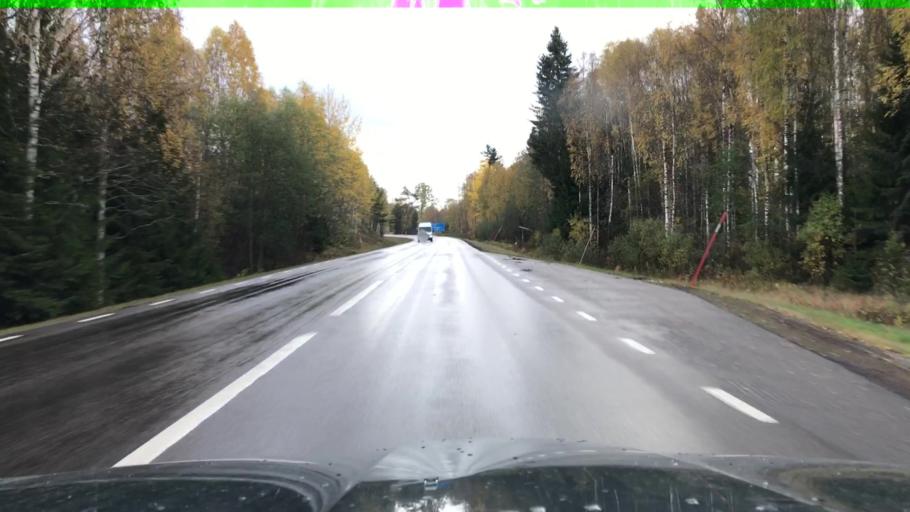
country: SE
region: Vaermland
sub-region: Hagfors Kommun
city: Ekshaerad
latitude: 60.4273
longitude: 13.2496
